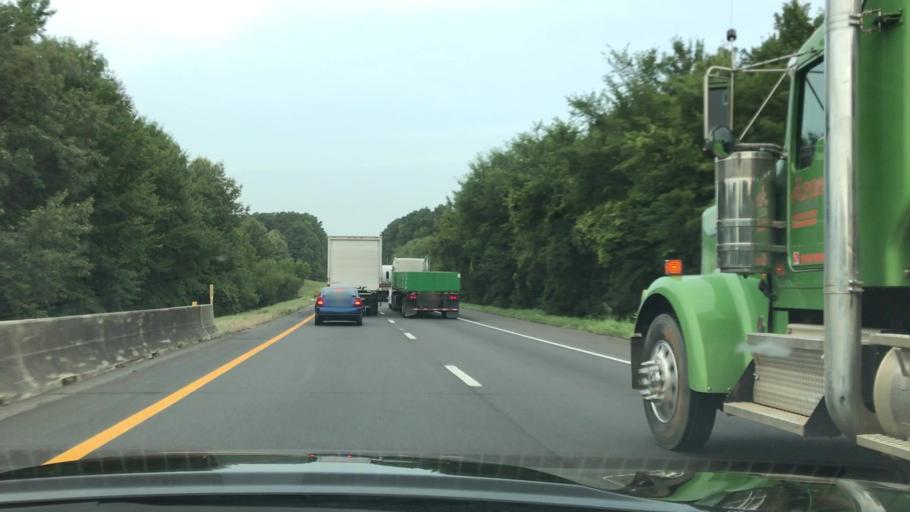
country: US
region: Texas
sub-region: Harrison County
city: Marshall
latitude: 32.4880
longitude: -94.4428
